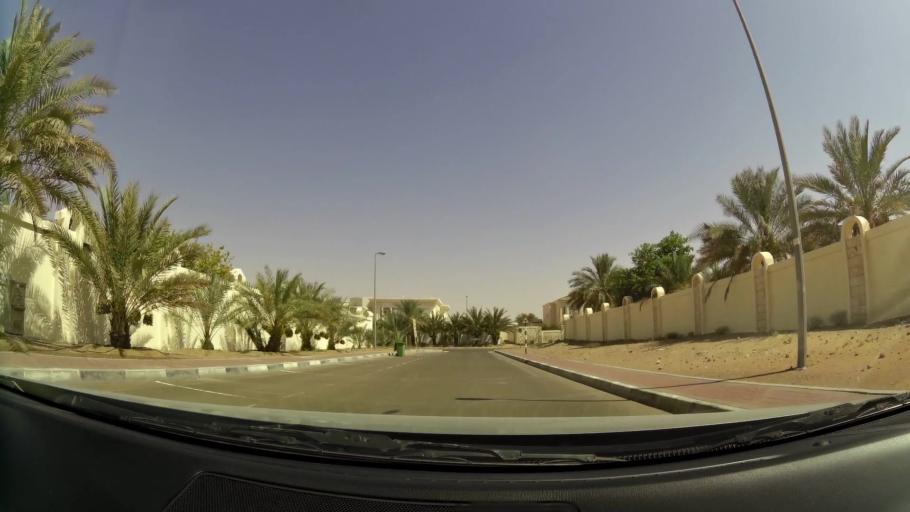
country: OM
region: Al Buraimi
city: Al Buraymi
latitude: 24.3018
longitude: 55.7575
